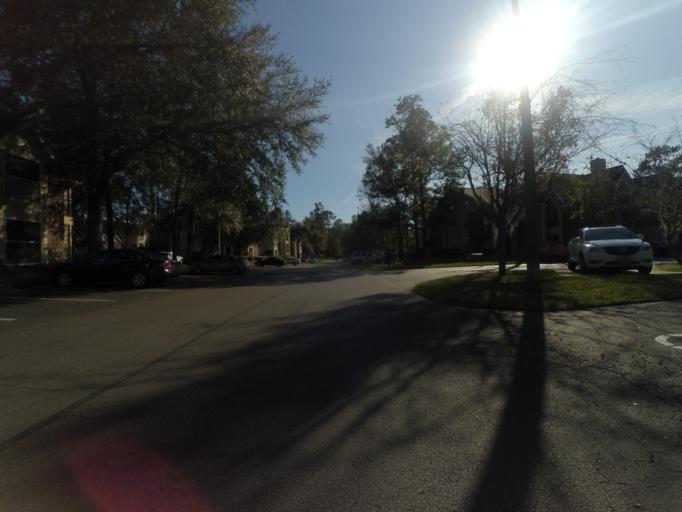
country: US
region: Florida
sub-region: Alachua County
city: Gainesville
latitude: 29.6155
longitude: -82.3574
